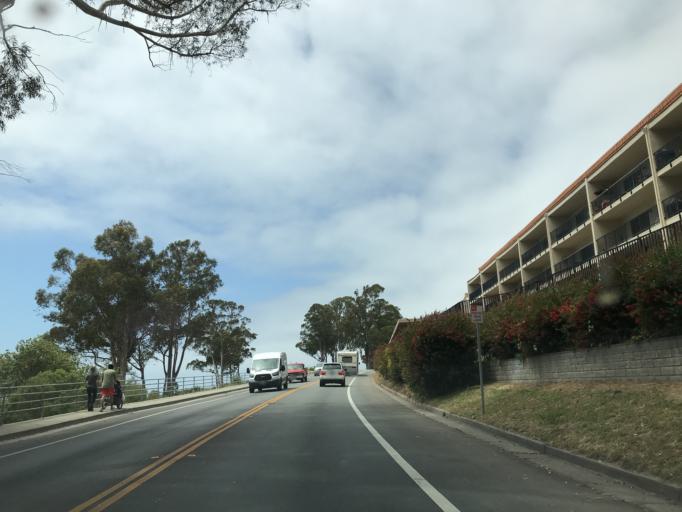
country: US
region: California
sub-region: Santa Cruz County
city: Capitola
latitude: 36.9795
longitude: -121.9391
